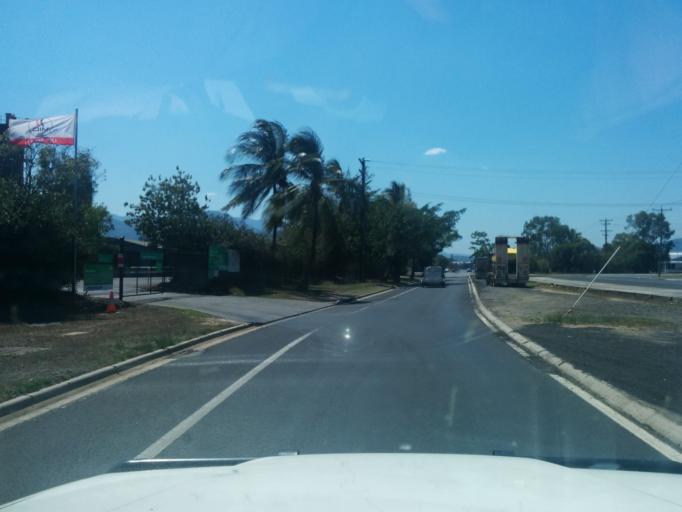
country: AU
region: Queensland
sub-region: Cairns
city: Cairns
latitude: -16.9443
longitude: 145.7712
